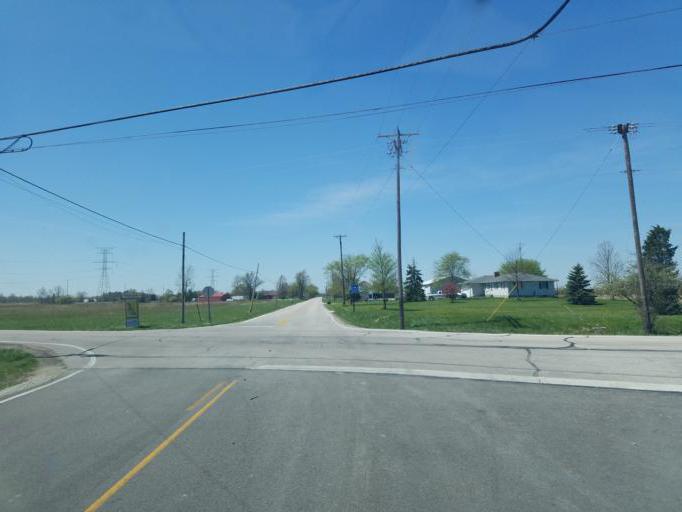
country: US
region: Ohio
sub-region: Ottawa County
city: Oak Harbor
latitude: 41.5921
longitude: -83.1447
